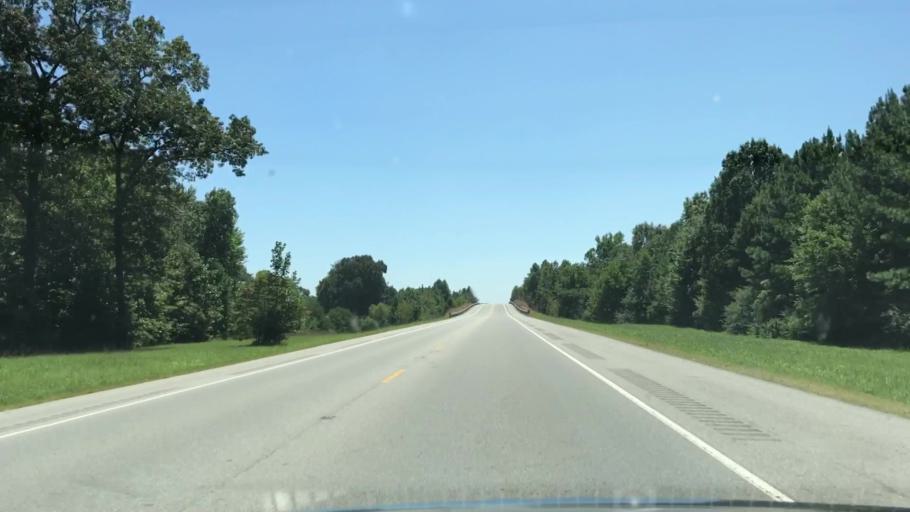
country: US
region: Tennessee
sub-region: Putnam County
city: Baxter
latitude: 36.1640
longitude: -85.6280
